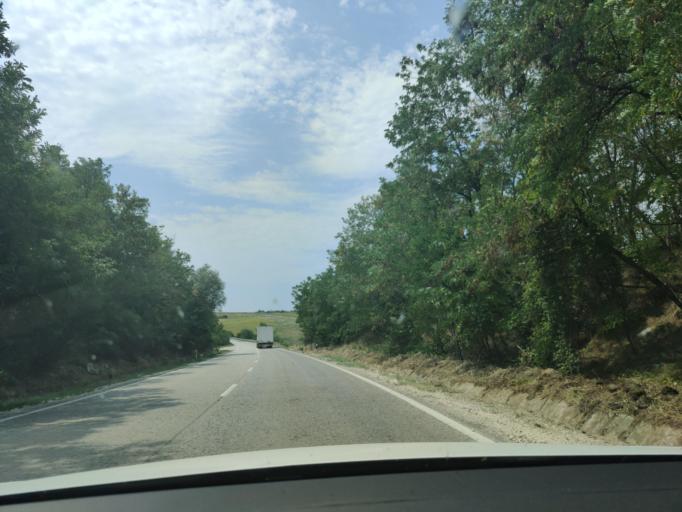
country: BG
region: Vidin
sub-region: Obshtina Vidin
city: Dunavtsi
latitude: 43.8762
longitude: 22.7864
